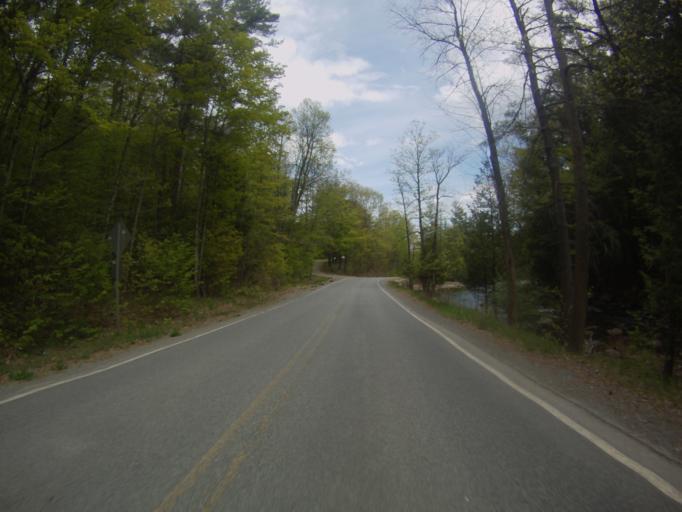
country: US
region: New York
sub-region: Essex County
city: Port Henry
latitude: 43.9423
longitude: -73.4812
